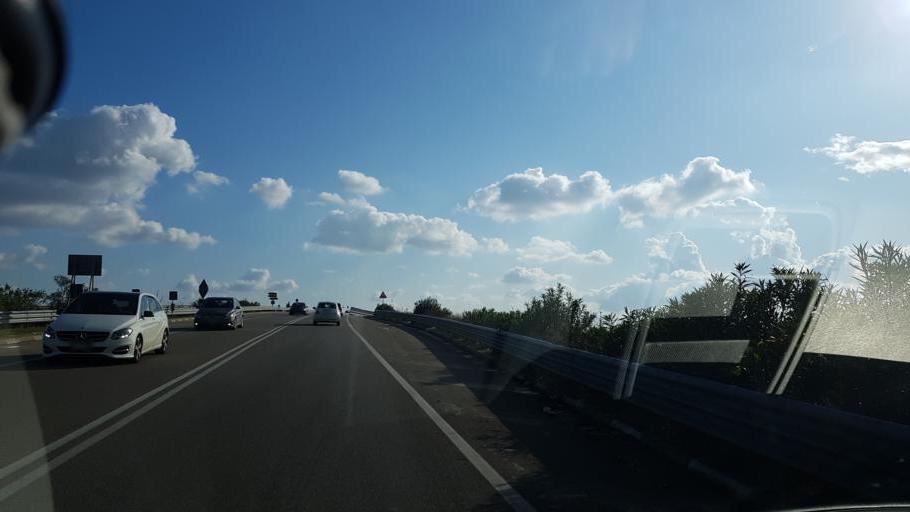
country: IT
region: Apulia
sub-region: Provincia di Lecce
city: Salice Salentino
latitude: 40.3902
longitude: 17.9685
